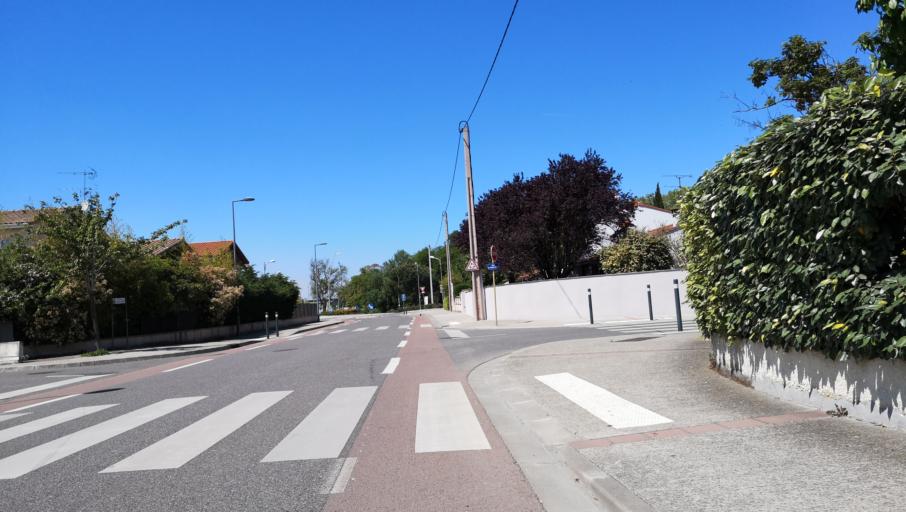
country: FR
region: Midi-Pyrenees
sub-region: Departement de la Haute-Garonne
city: Blagnac
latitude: 43.6504
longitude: 1.3858
